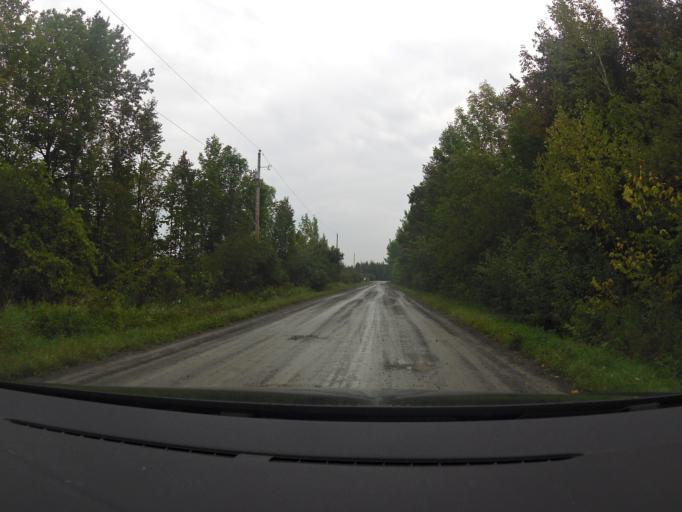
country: CA
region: Ontario
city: Carleton Place
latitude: 45.1824
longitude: -76.0678
